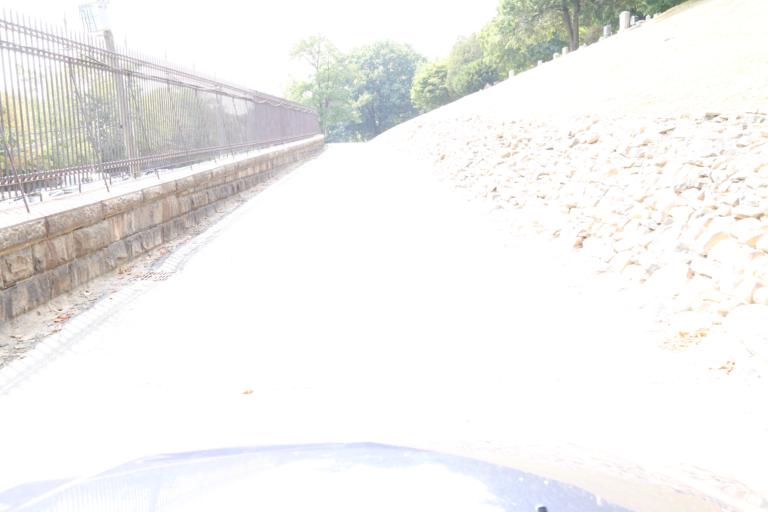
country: US
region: New York
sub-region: Bronx
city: Eastchester
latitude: 40.8883
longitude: -73.8676
